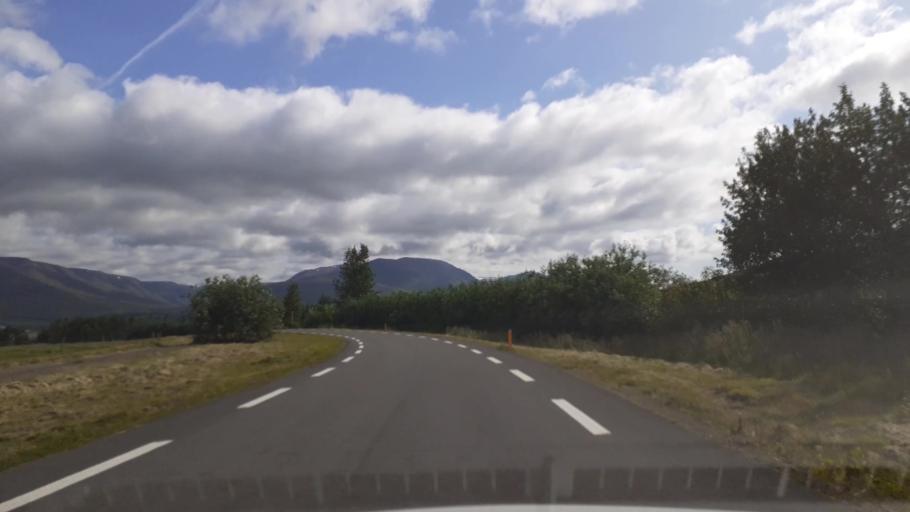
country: IS
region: Northeast
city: Akureyri
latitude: 65.6502
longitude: -18.0917
